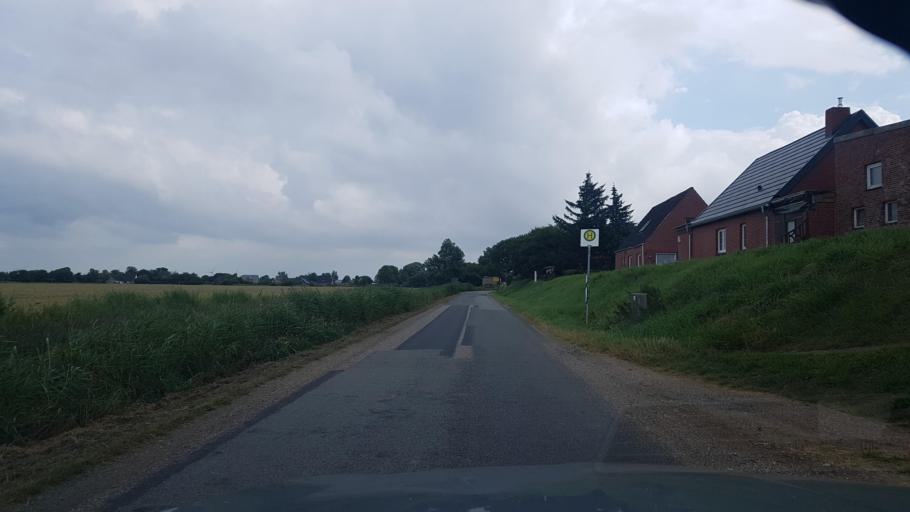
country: DE
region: Schleswig-Holstein
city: Elisabeth-Sophien-Koog
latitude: 54.4831
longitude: 8.8426
